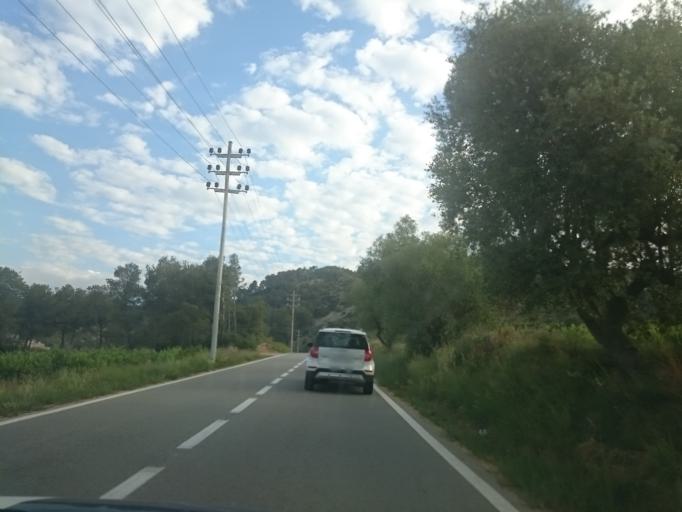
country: ES
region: Catalonia
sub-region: Provincia de Barcelona
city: Castellet
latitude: 41.2524
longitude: 1.6564
